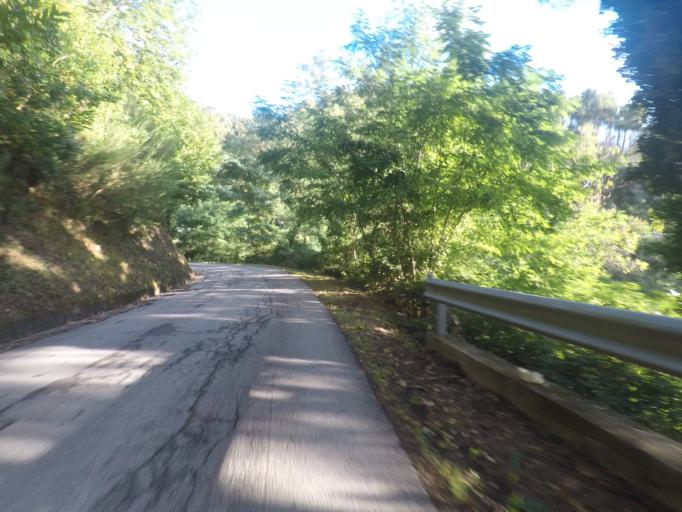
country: IT
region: Tuscany
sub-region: Provincia di Lucca
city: Stiava
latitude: 43.9143
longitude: 10.3668
